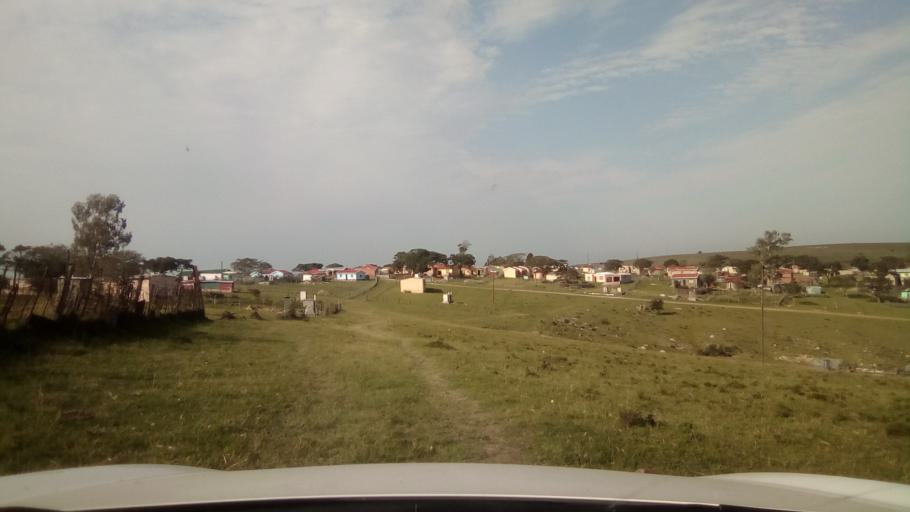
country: ZA
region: Eastern Cape
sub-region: Buffalo City Metropolitan Municipality
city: Bhisho
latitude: -33.0068
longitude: 27.3033
